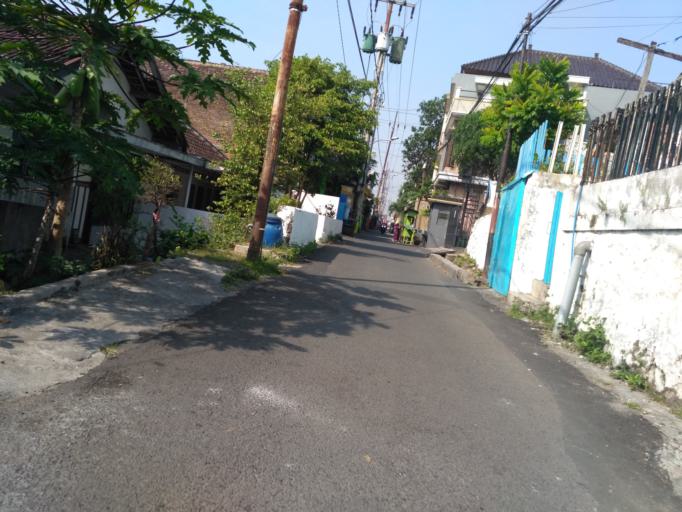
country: ID
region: East Java
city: Malang
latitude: -7.9804
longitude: 112.6225
